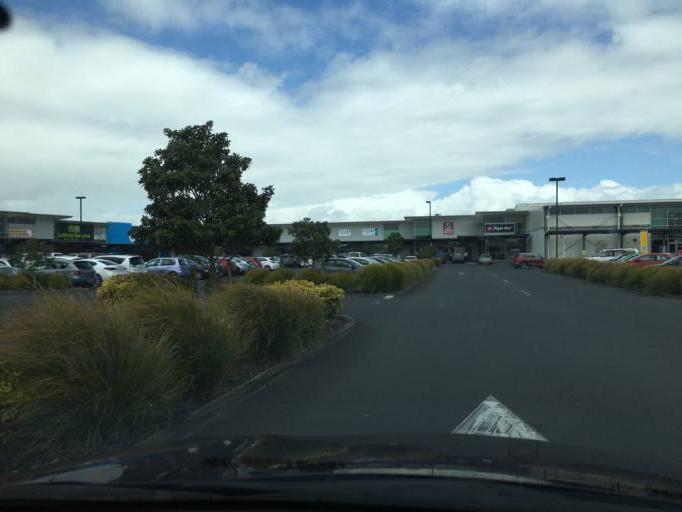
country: NZ
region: Waikato
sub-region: Waipa District
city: Cambridge
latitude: -38.0073
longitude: 175.3401
